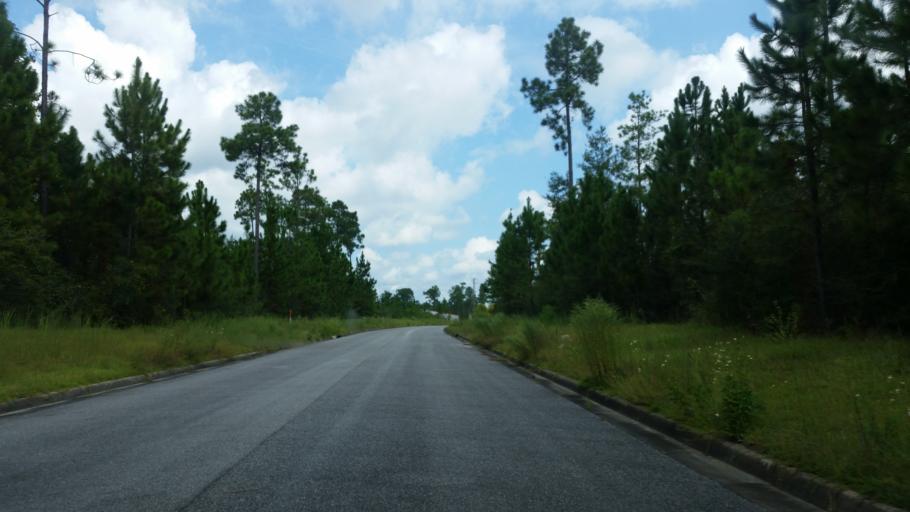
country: US
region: Florida
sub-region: Escambia County
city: Cantonment
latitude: 30.6434
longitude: -87.3503
